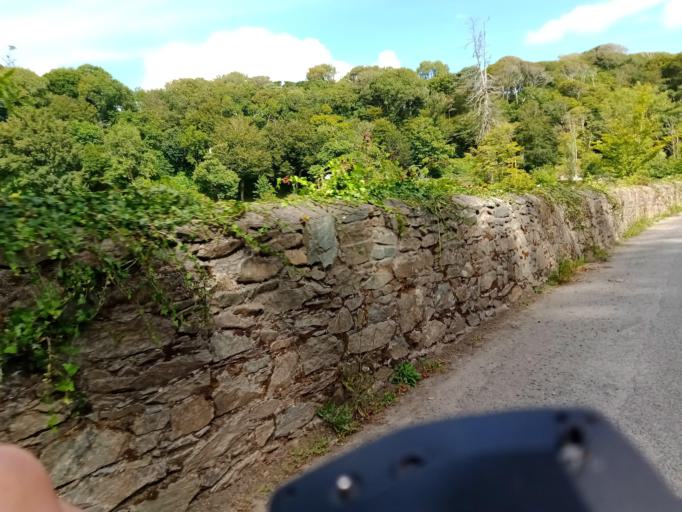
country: IE
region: Munster
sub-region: Waterford
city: Dungarvan
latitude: 52.1251
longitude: -7.4631
